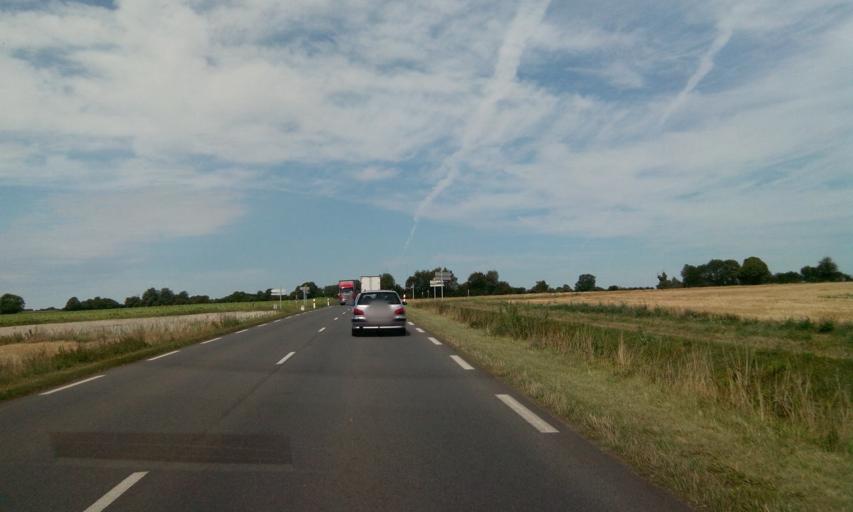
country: FR
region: Poitou-Charentes
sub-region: Departement des Deux-Sevres
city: Lezay
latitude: 46.1683
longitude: 0.0113
